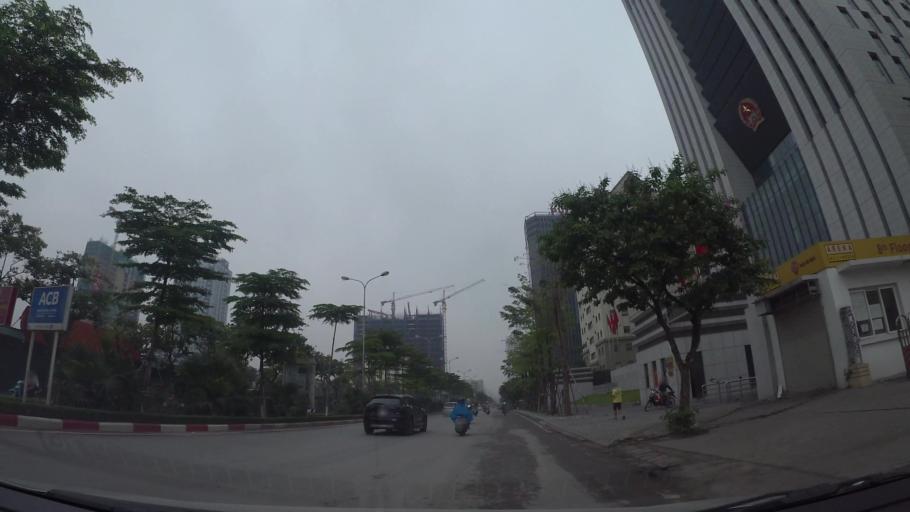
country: VN
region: Ha Noi
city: Cau Giay
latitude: 21.0259
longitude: 105.7883
